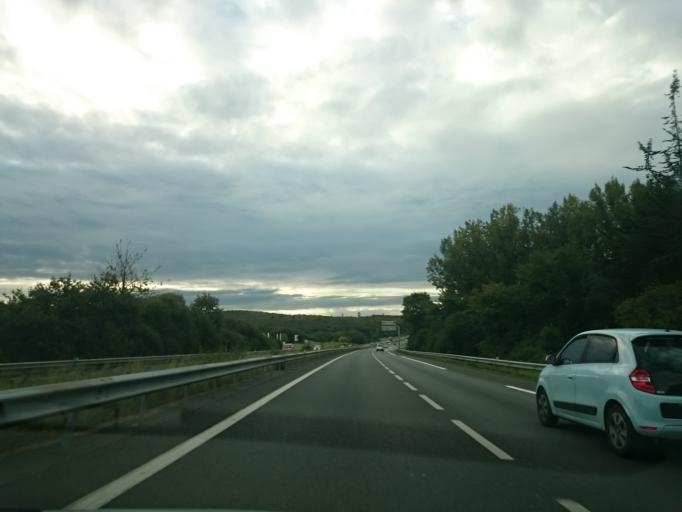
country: FR
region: Brittany
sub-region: Departement du Finistere
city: Le Faou
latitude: 48.2998
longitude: -4.1757
